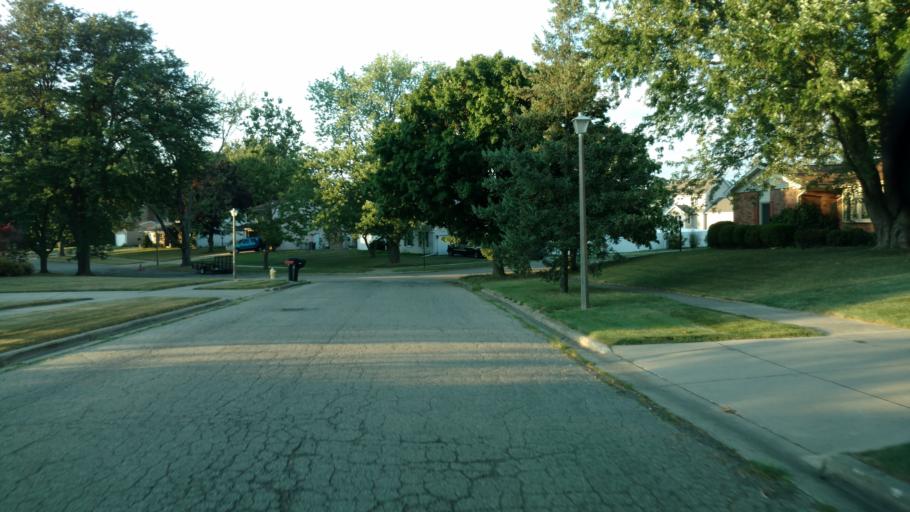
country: US
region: Michigan
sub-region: Eaton County
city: Waverly
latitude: 42.7227
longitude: -84.6283
